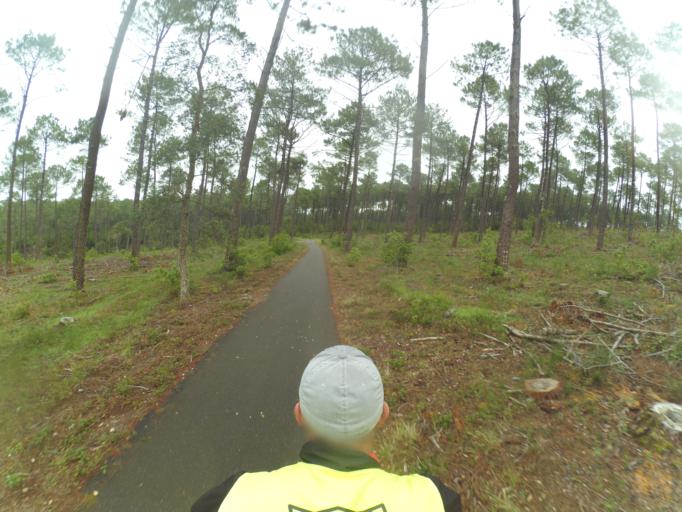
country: FR
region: Aquitaine
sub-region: Departement des Landes
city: Mimizan
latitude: 44.2202
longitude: -1.2508
